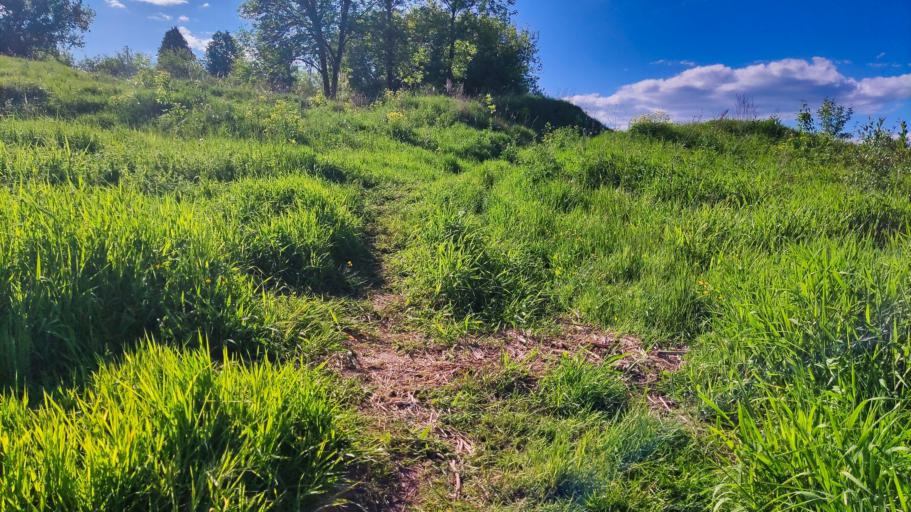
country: RU
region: Tverskaya
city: Rzhev
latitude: 56.2510
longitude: 34.3475
